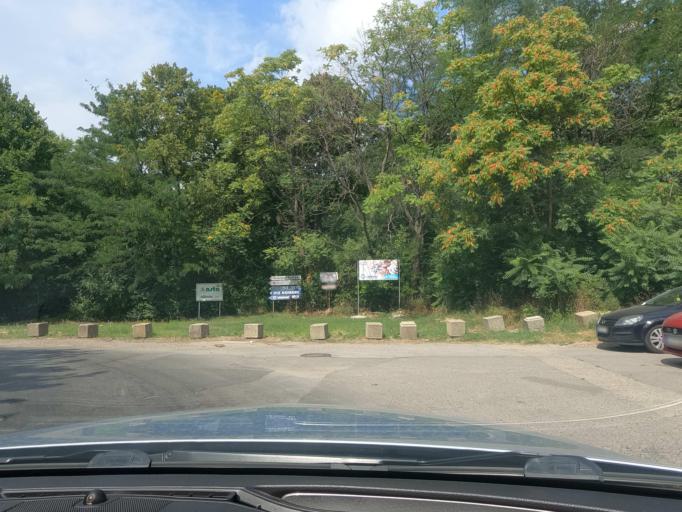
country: RS
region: Central Serbia
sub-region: Belgrade
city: Zemun
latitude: 44.8280
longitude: 20.3828
